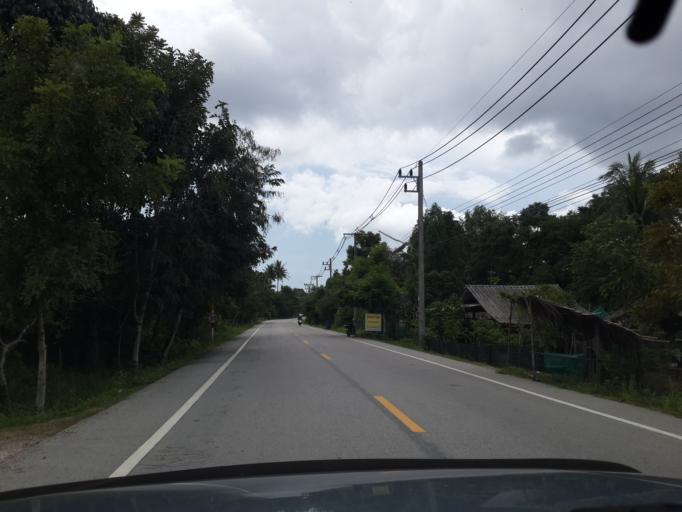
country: TH
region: Narathiwat
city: Narathiwat
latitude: 6.4800
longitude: 101.7764
